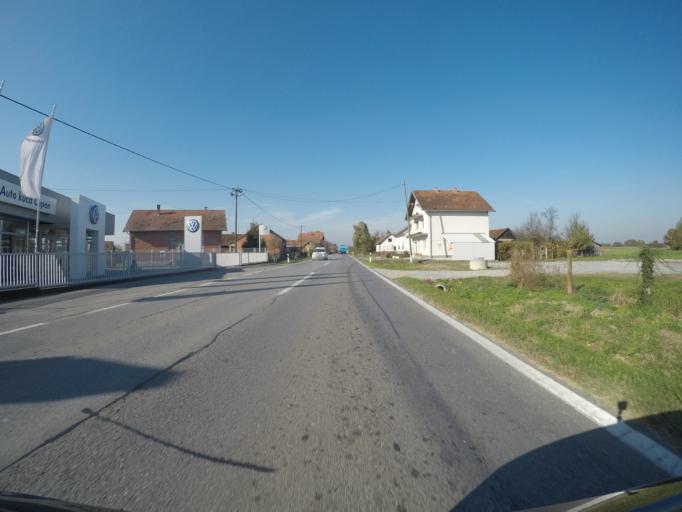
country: HR
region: Bjelovarsko-Bilogorska
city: Predavac
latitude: 45.9273
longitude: 16.7868
